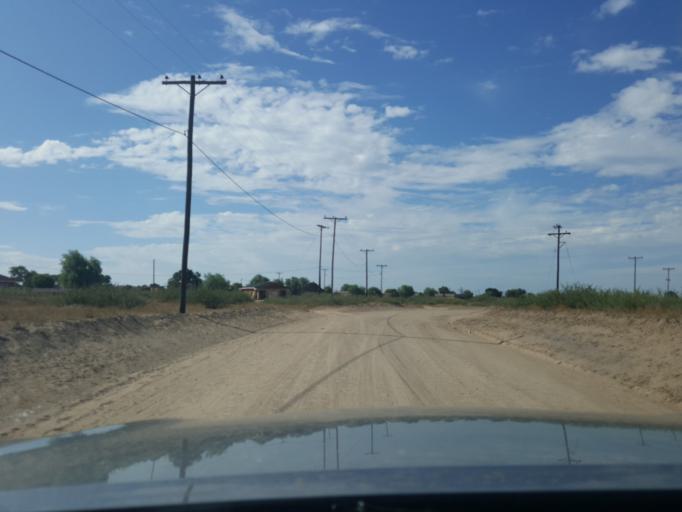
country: BW
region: Kweneng
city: Khudumelapye
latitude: -23.6927
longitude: 24.7170
